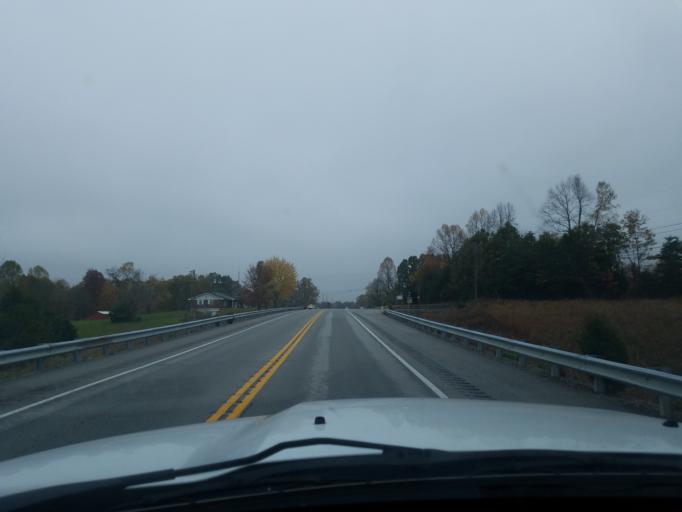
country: US
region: Kentucky
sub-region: Green County
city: Greensburg
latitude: 37.4077
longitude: -85.4837
